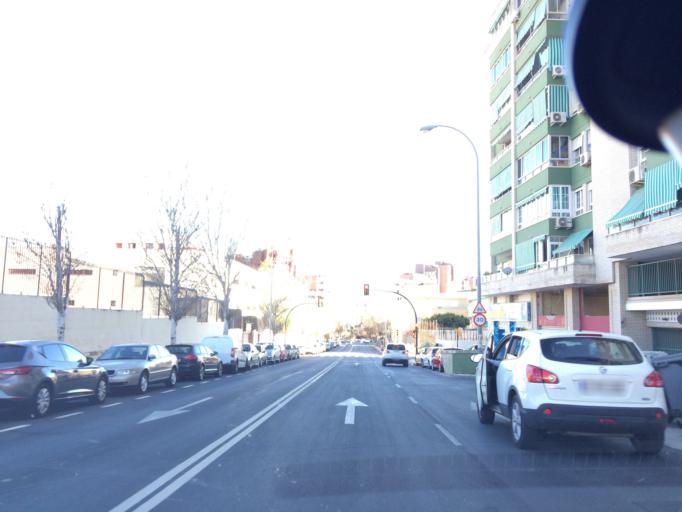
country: ES
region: Andalusia
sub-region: Provincia de Malaga
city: Malaga
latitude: 36.7254
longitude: -4.4424
